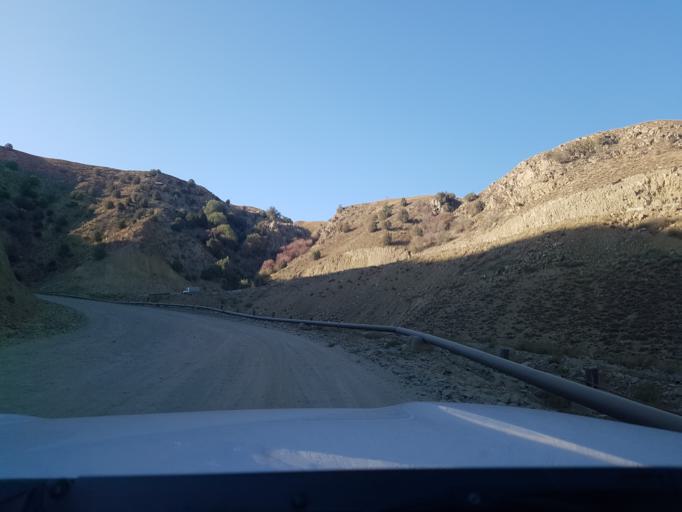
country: TM
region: Ahal
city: Baharly
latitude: 38.4432
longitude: 57.0476
